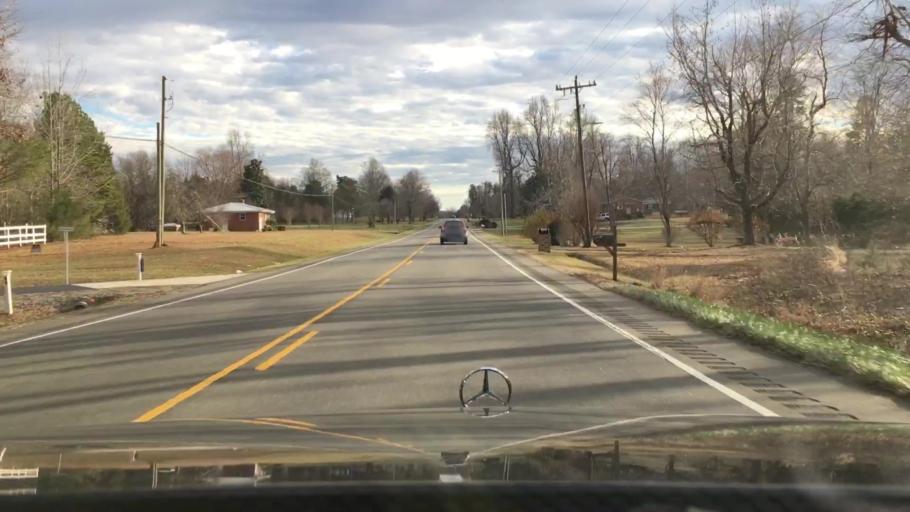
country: US
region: North Carolina
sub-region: Orange County
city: Hillsborough
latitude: 36.1829
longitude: -79.1369
